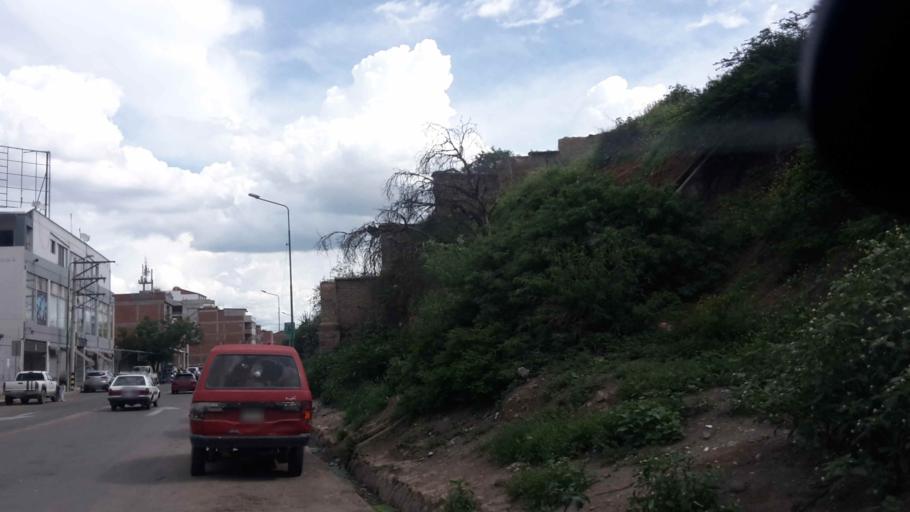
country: BO
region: Cochabamba
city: Cochabamba
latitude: -17.4060
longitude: -66.1576
